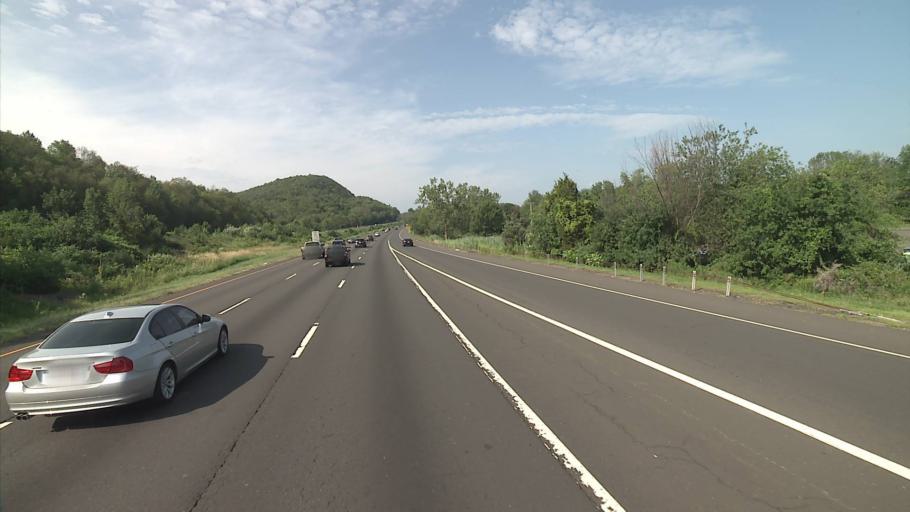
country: US
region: Connecticut
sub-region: Middlesex County
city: Middletown
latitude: 41.5683
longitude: -72.7273
